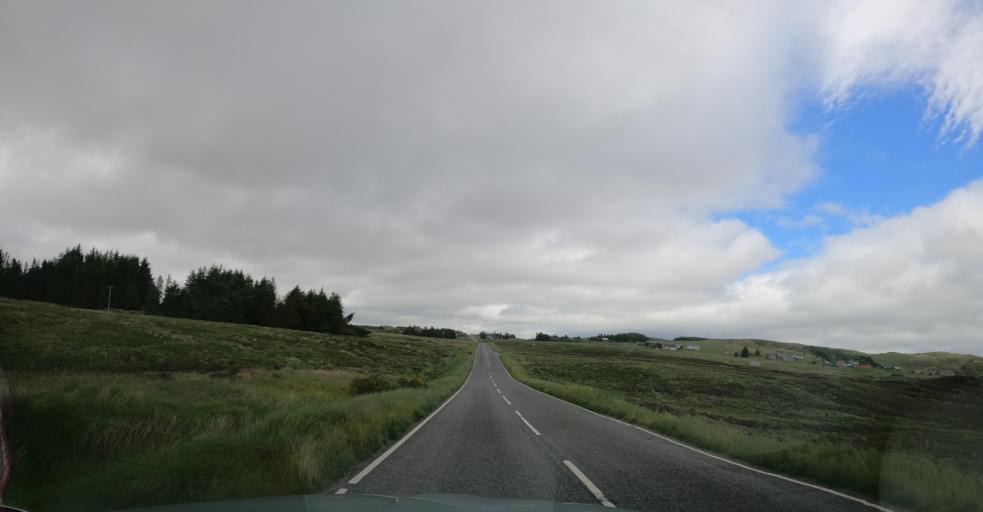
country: GB
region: Scotland
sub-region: Eilean Siar
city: Stornoway
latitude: 58.1467
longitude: -6.5075
